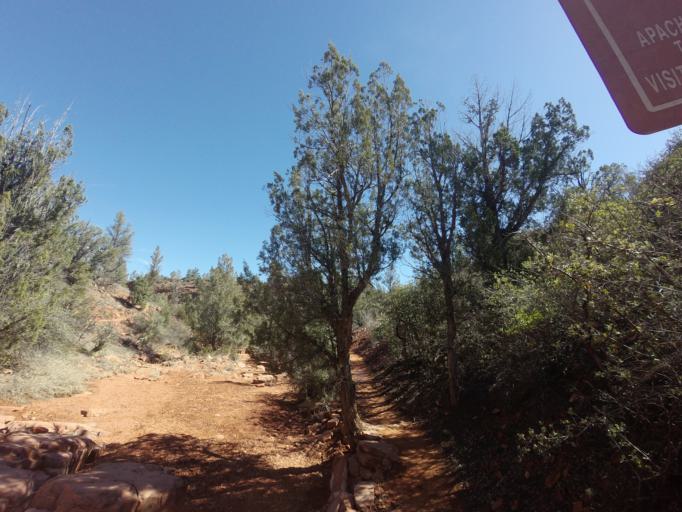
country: US
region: Arizona
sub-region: Yavapai County
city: West Sedona
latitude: 34.8066
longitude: -111.8238
